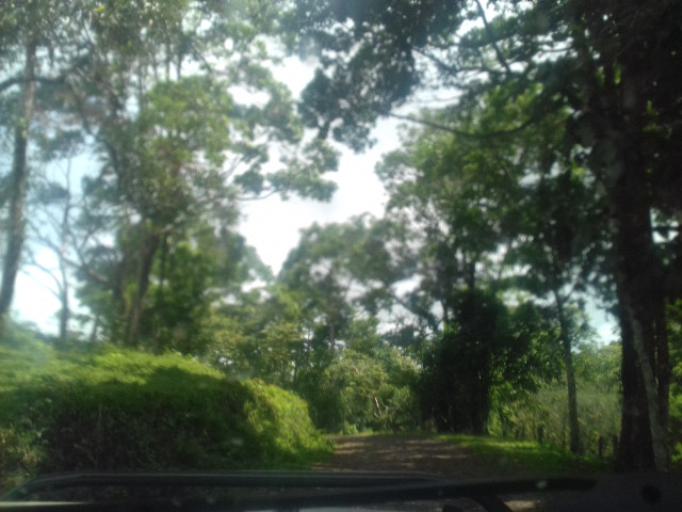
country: NI
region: Matagalpa
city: Matiguas
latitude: 12.9304
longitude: -85.3659
